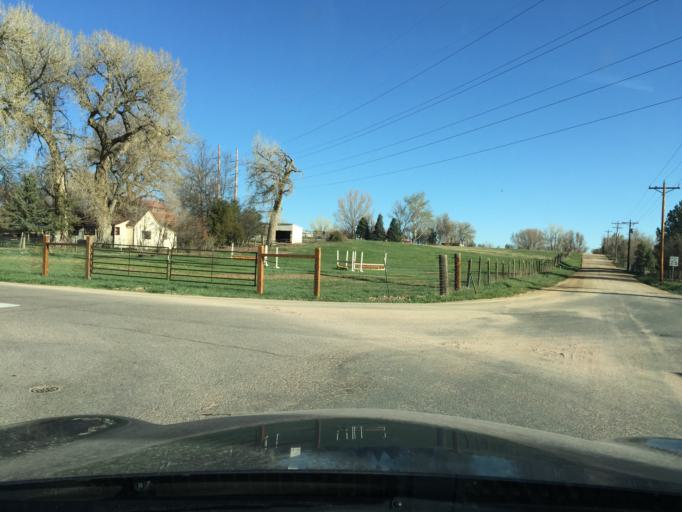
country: US
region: Colorado
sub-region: Boulder County
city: Erie
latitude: 40.0728
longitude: -105.0837
